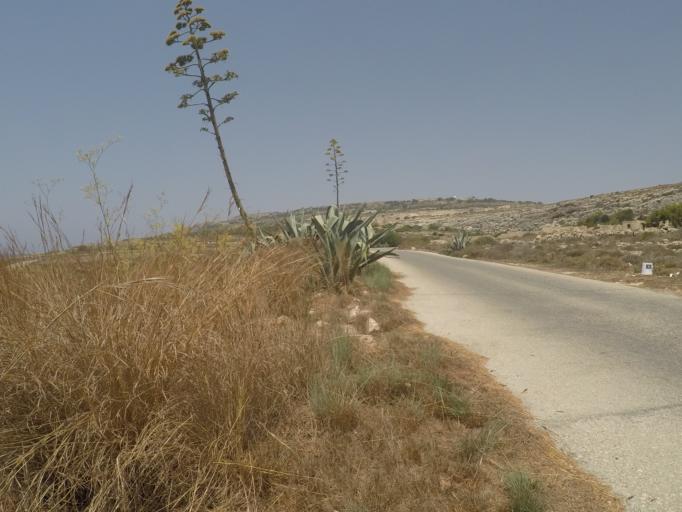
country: MT
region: Is-Siggiewi
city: Siggiewi
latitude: 35.8288
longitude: 14.4212
